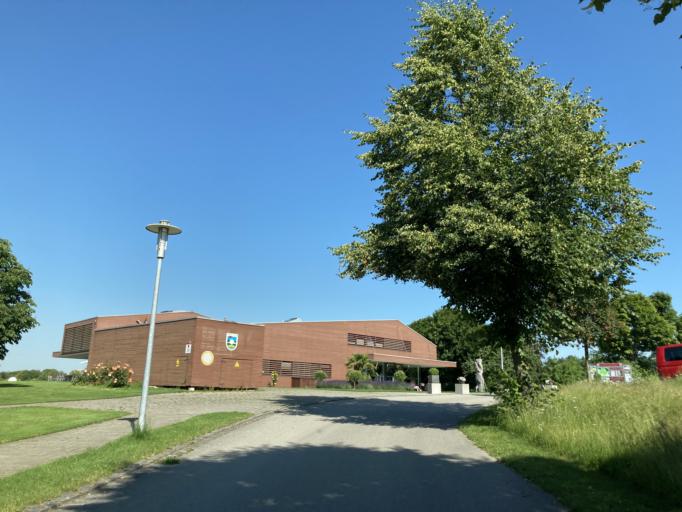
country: DE
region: Bavaria
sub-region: Upper Bavaria
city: Hoslwang
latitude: 47.9656
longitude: 12.3357
